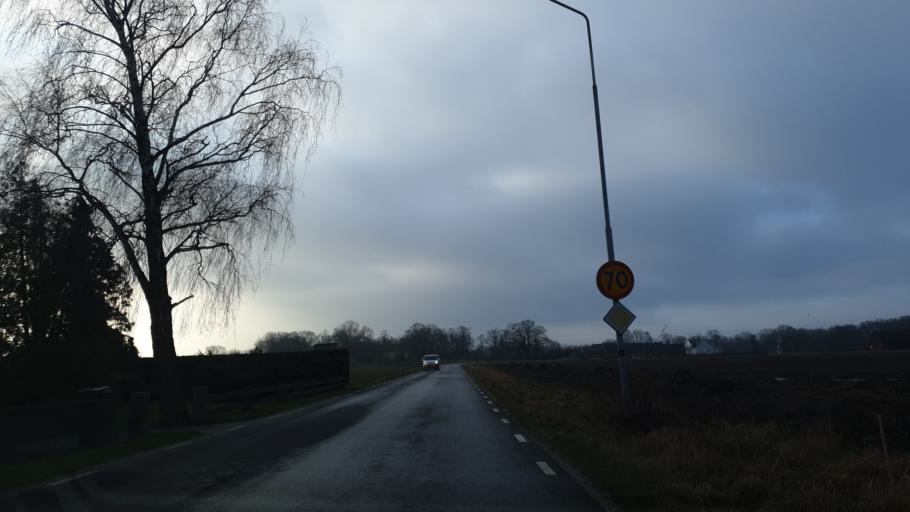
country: SE
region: Blekinge
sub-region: Karlshamns Kommun
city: Morrum
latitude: 56.1658
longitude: 14.7582
